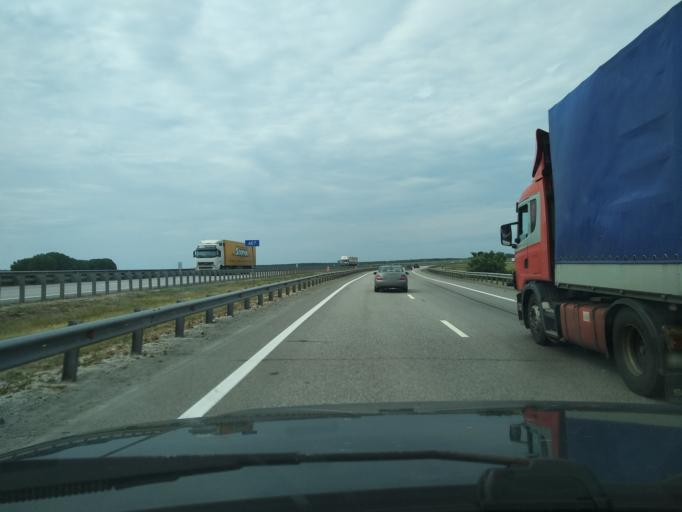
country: RU
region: Lipetsk
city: Khlevnoye
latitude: 52.0641
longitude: 39.1802
